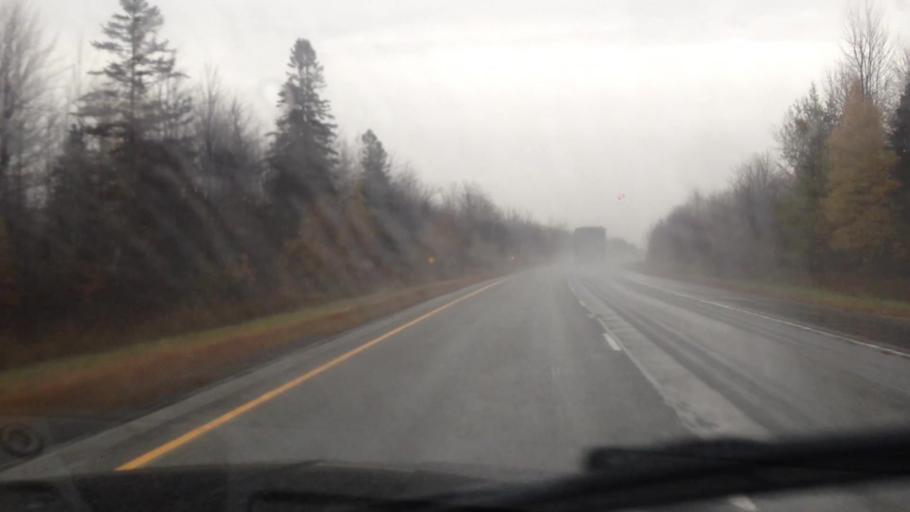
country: CA
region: Ontario
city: Casselman
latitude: 45.3143
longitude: -75.1966
